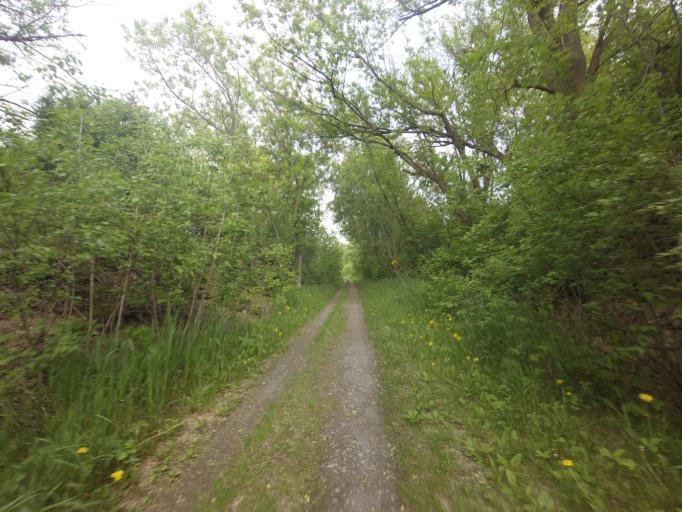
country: CA
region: Ontario
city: Kingston
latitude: 44.4096
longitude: -76.6051
